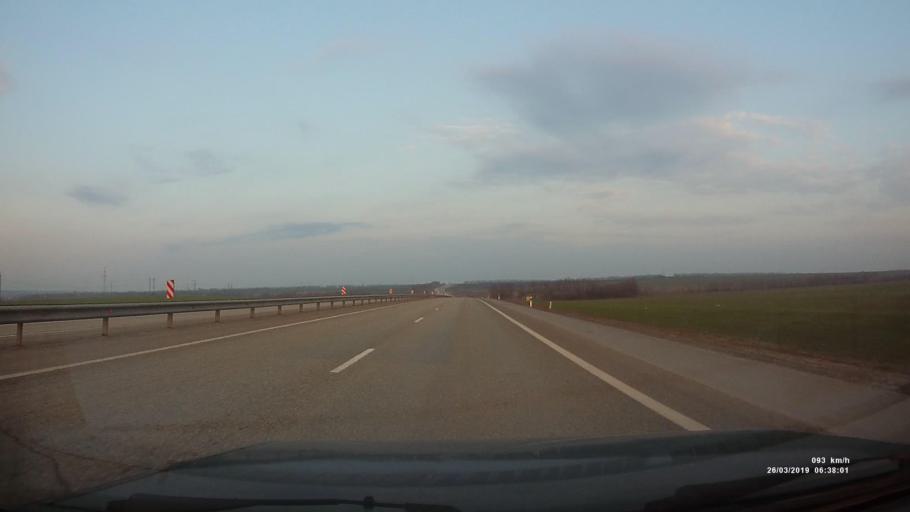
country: RU
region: Rostov
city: Chaltyr
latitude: 47.2842
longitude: 39.3918
